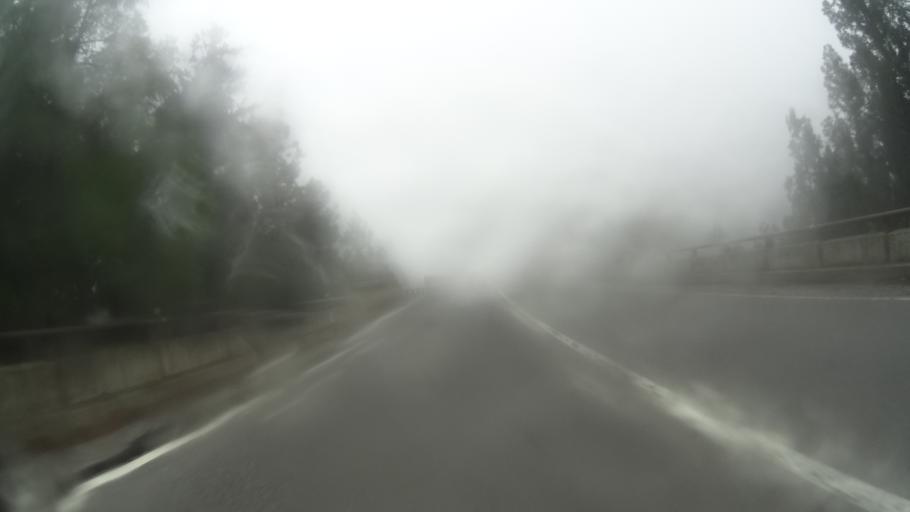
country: JP
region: Nagano
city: Nakano
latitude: 36.7217
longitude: 138.4508
